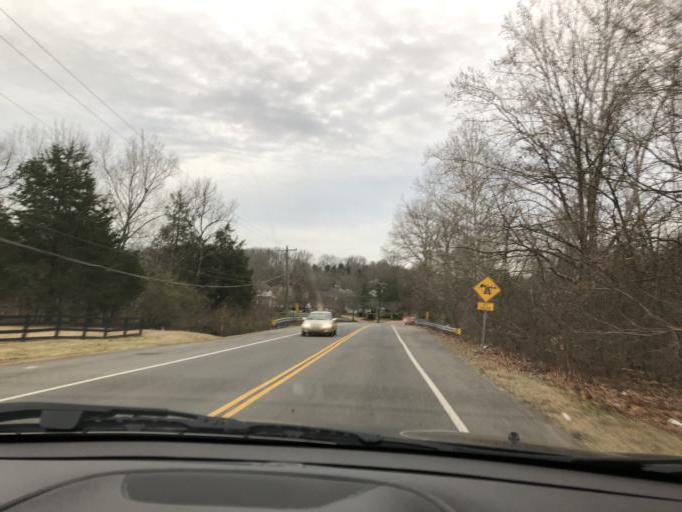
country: US
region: Tennessee
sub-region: Wilson County
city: Green Hill
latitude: 36.2024
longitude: -86.5917
